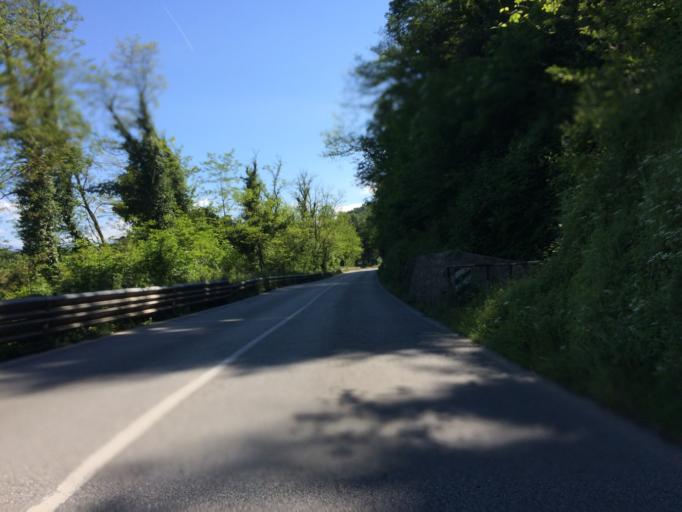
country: IT
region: Tuscany
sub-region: Provincia di Massa-Carrara
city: Montale
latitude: 44.1947
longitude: 9.9486
